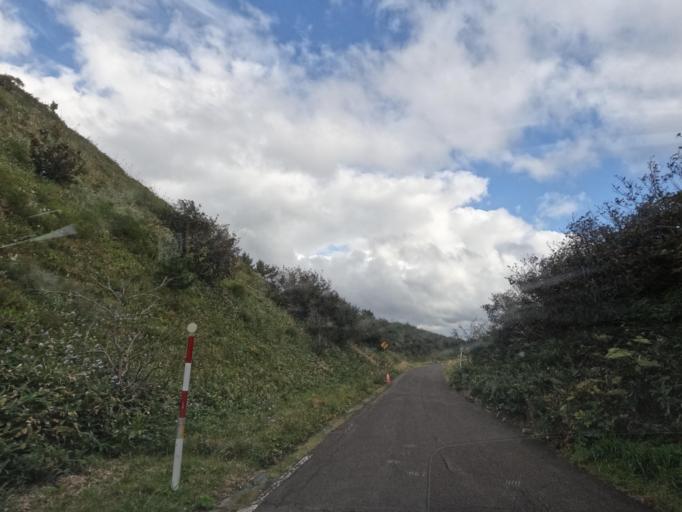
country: JP
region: Hokkaido
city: Muroran
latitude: 42.3188
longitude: 141.0060
